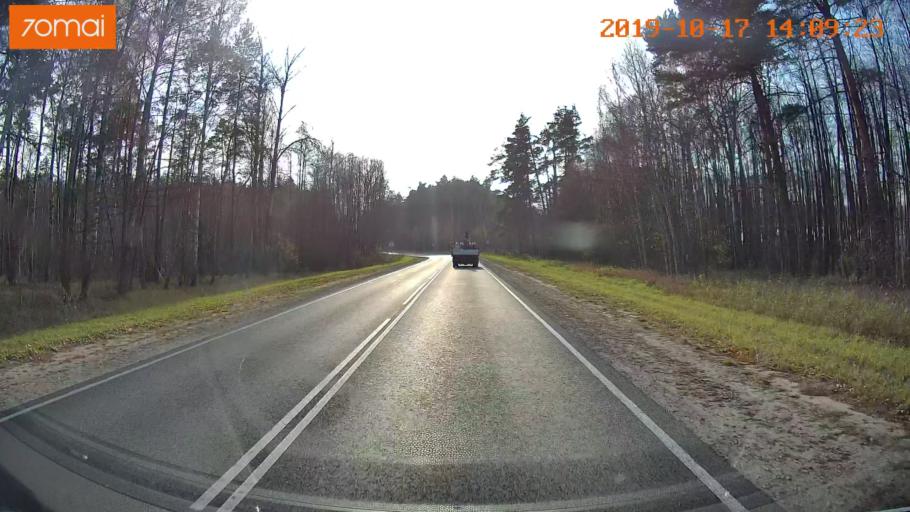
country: RU
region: Rjazan
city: Spas-Klepiki
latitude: 55.0896
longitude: 40.0582
